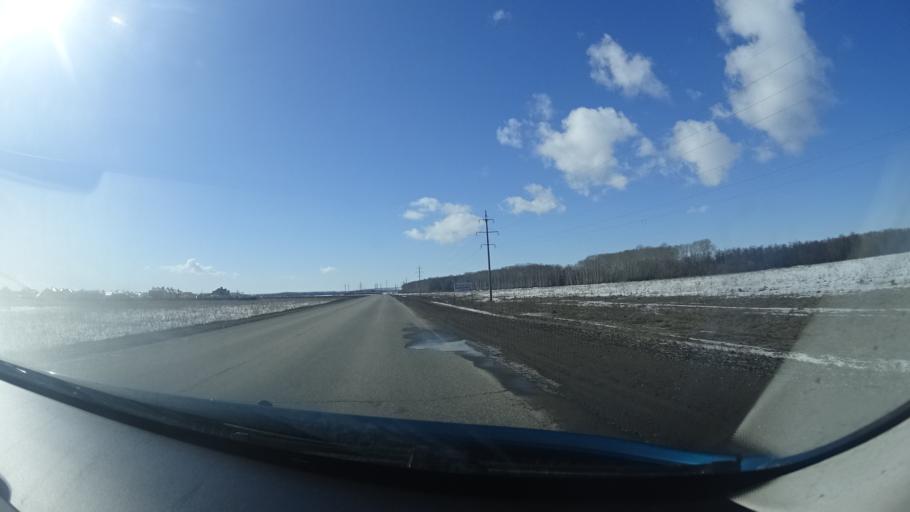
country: RU
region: Bashkortostan
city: Ufa
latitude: 54.6310
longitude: 55.9016
